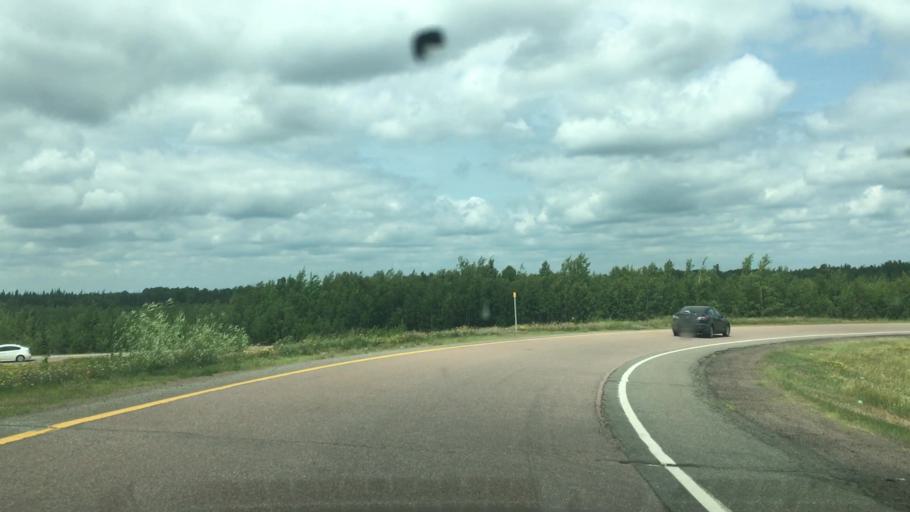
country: CA
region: New Brunswick
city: Dieppe
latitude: 46.1285
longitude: -64.6831
